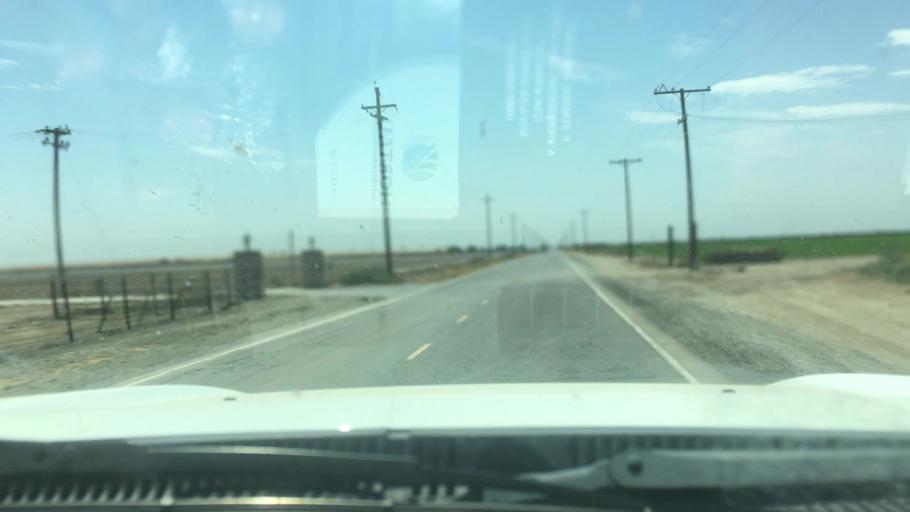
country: US
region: California
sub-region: Kings County
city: Corcoran
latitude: 36.0508
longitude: -119.4462
